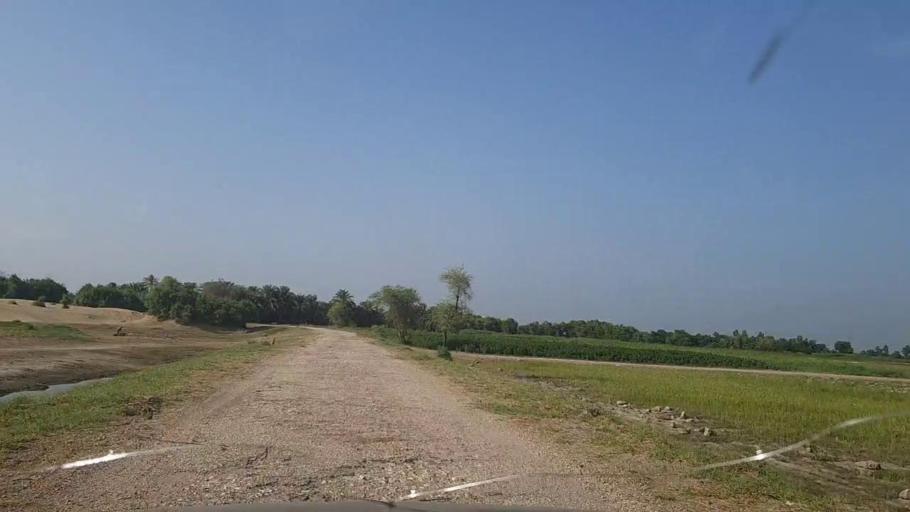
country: PK
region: Sindh
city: Khanpur
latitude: 27.7228
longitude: 69.3318
